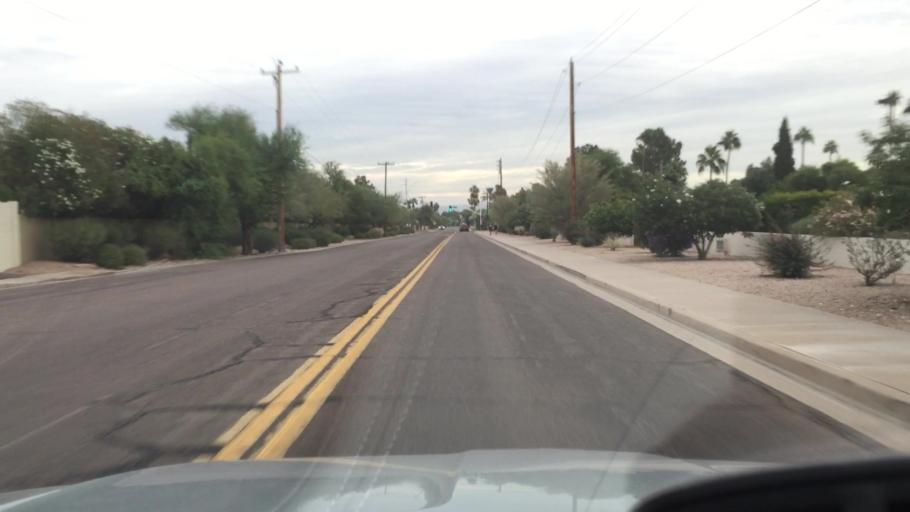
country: US
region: Arizona
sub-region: Maricopa County
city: Paradise Valley
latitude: 33.5094
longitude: -111.9372
